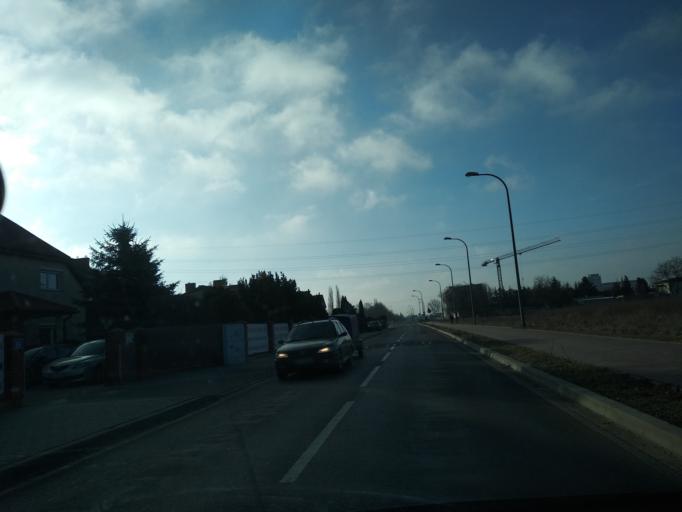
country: PL
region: Masovian Voivodeship
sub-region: Powiat piaseczynski
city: Mysiadlo
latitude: 52.0902
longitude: 21.0128
